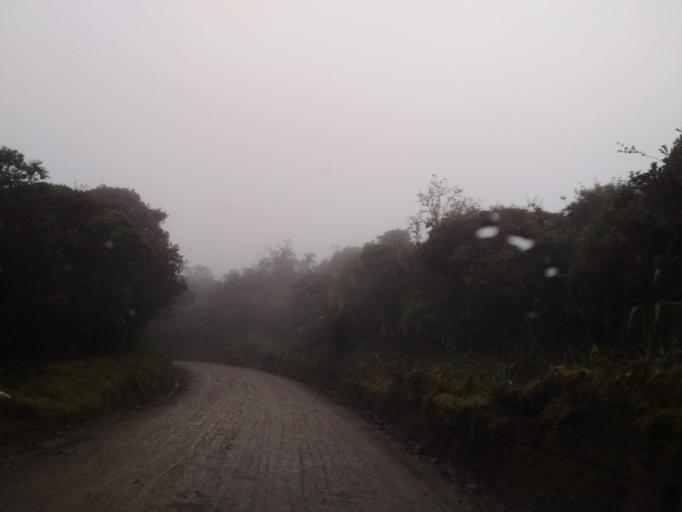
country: CO
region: Cauca
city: Paispamba
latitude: 2.1511
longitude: -76.4259
